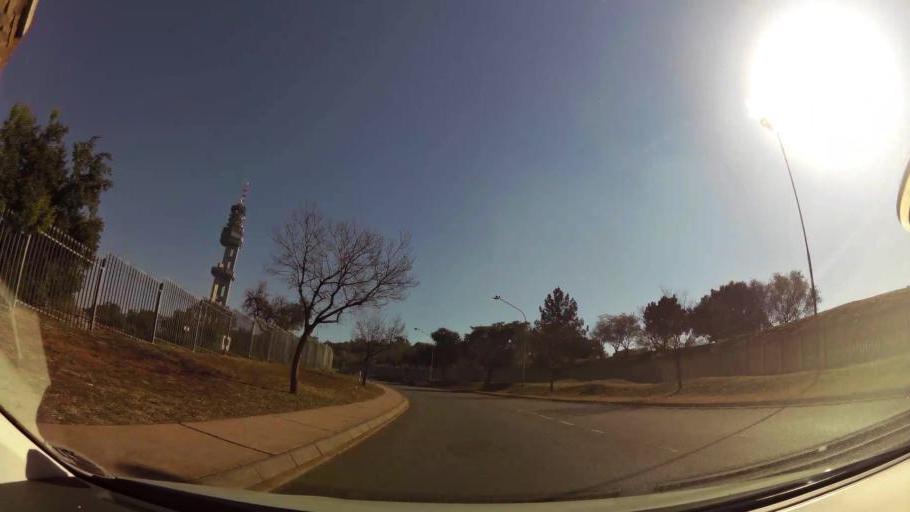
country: ZA
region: Gauteng
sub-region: City of Tshwane Metropolitan Municipality
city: Pretoria
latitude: -25.7680
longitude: 28.2095
